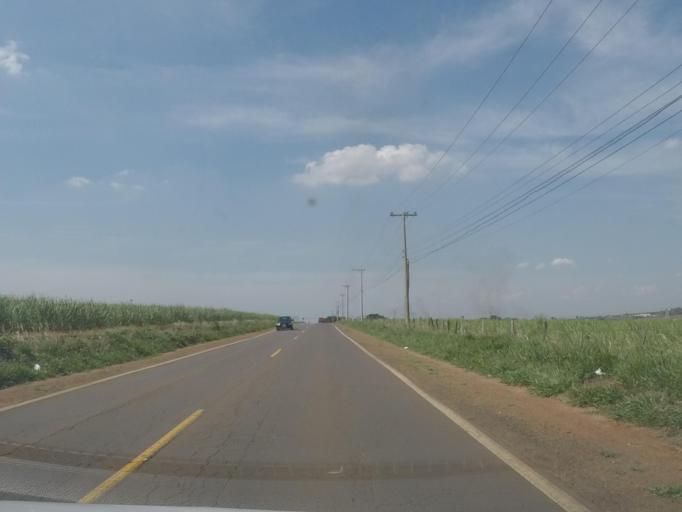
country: BR
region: Sao Paulo
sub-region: Sumare
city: Sumare
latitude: -22.8719
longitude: -47.2984
